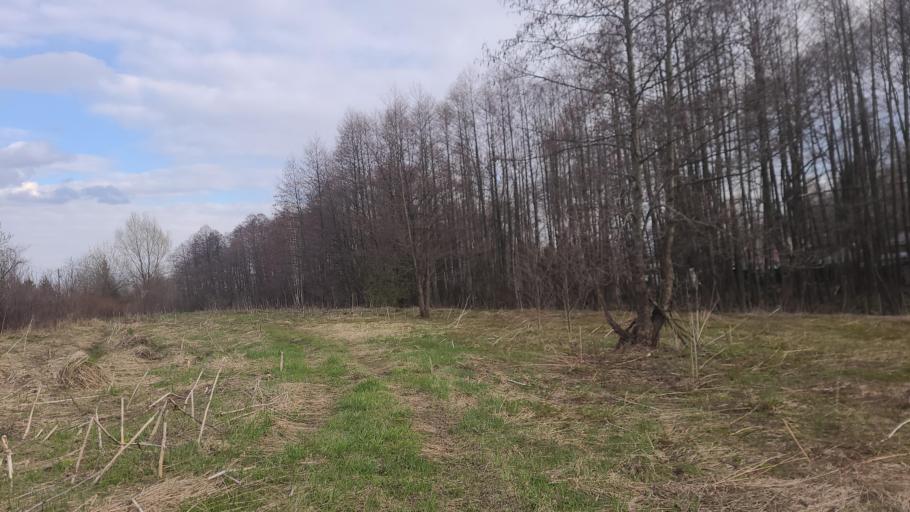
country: RU
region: Moskovskaya
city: Belyye Stolby
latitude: 55.3178
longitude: 37.8780
